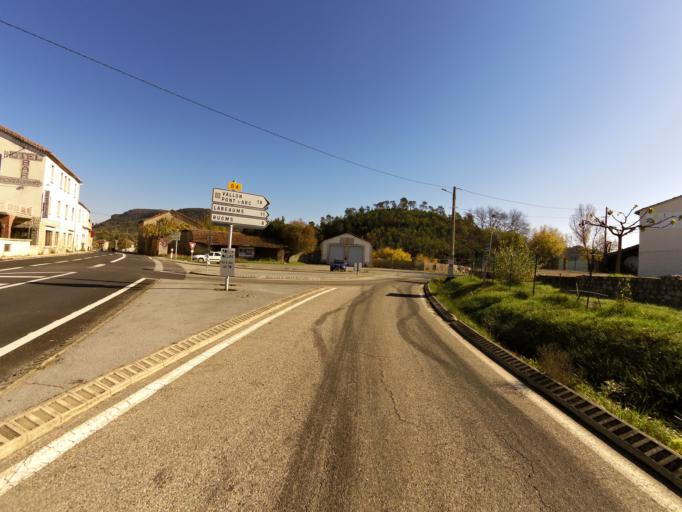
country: FR
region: Rhone-Alpes
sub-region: Departement de l'Ardeche
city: Largentiere
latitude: 44.5048
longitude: 4.3095
